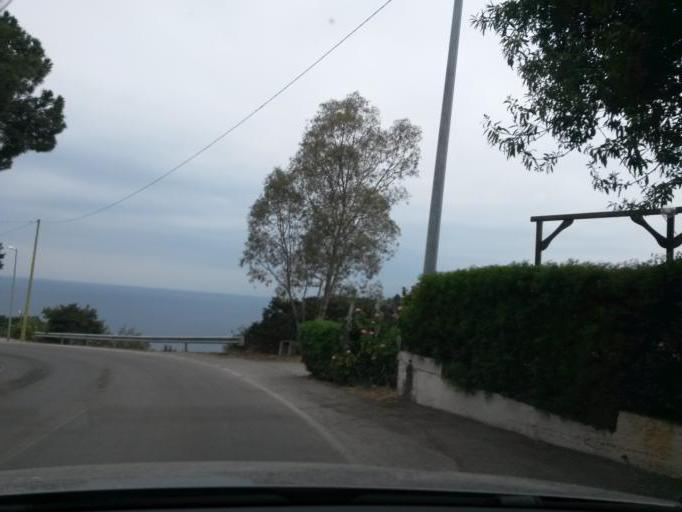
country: IT
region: Tuscany
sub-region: Provincia di Livorno
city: Capoliveri
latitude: 42.7321
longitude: 10.3761
